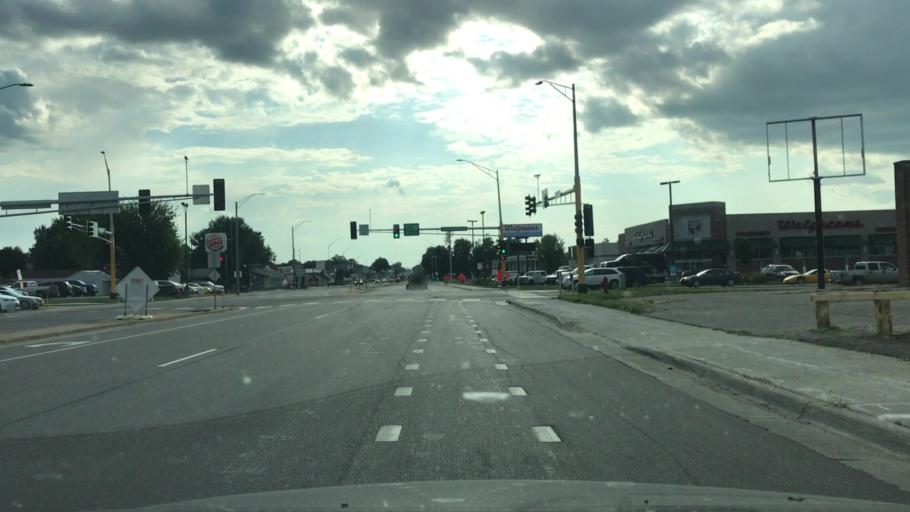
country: US
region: Minnesota
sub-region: Nobles County
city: Worthington
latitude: 43.6313
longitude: -95.5928
